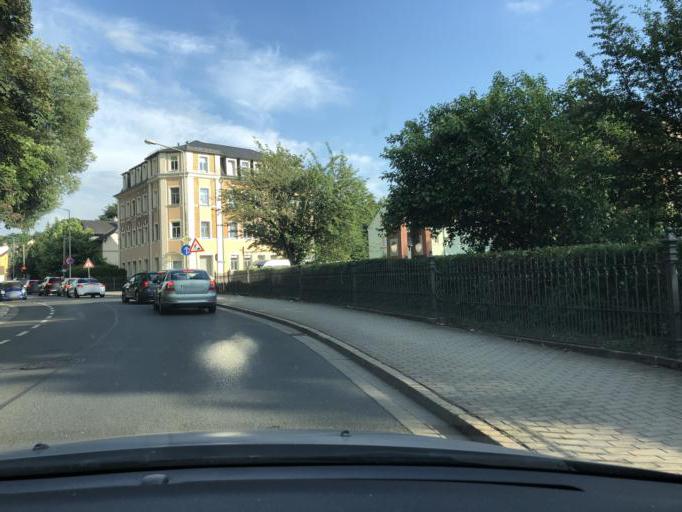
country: DE
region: Saxony
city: Freital
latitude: 50.9945
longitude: 13.6539
